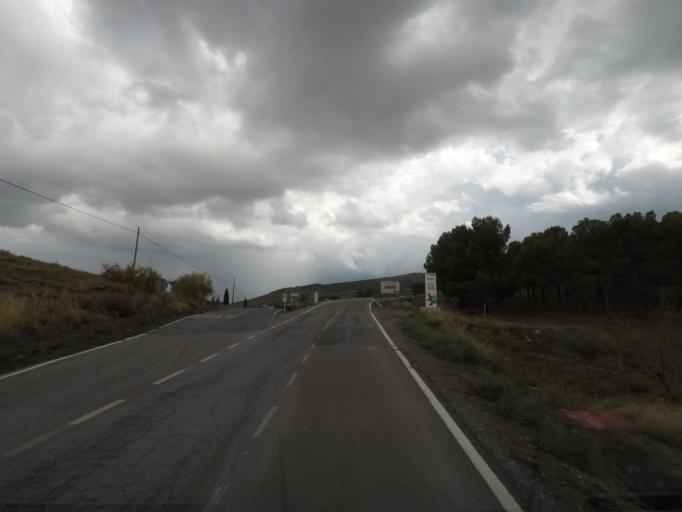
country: ES
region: Andalusia
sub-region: Provincia de Granada
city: Ferreira
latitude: 37.1751
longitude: -3.0480
